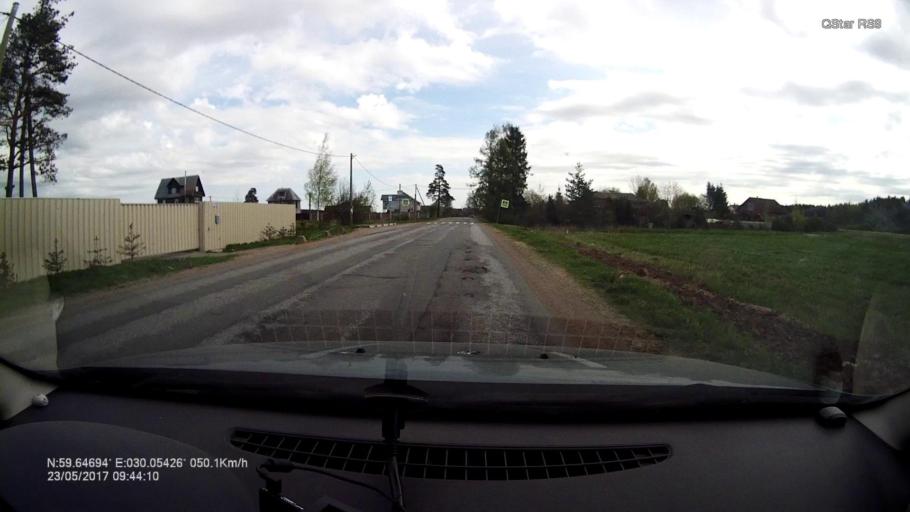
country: RU
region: Leningrad
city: Taytsy
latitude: 59.6470
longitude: 30.0544
